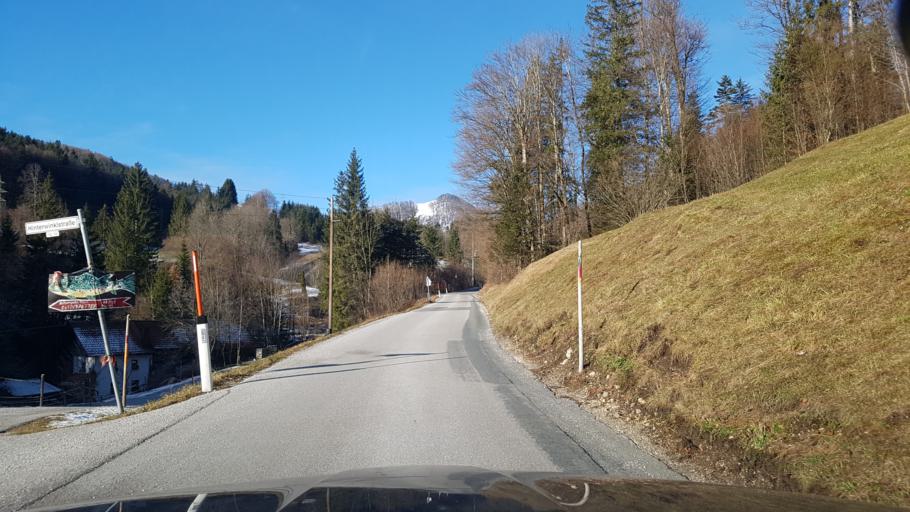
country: AT
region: Salzburg
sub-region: Politischer Bezirk Salzburg-Umgebung
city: Ebenau
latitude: 47.7685
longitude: 13.1739
